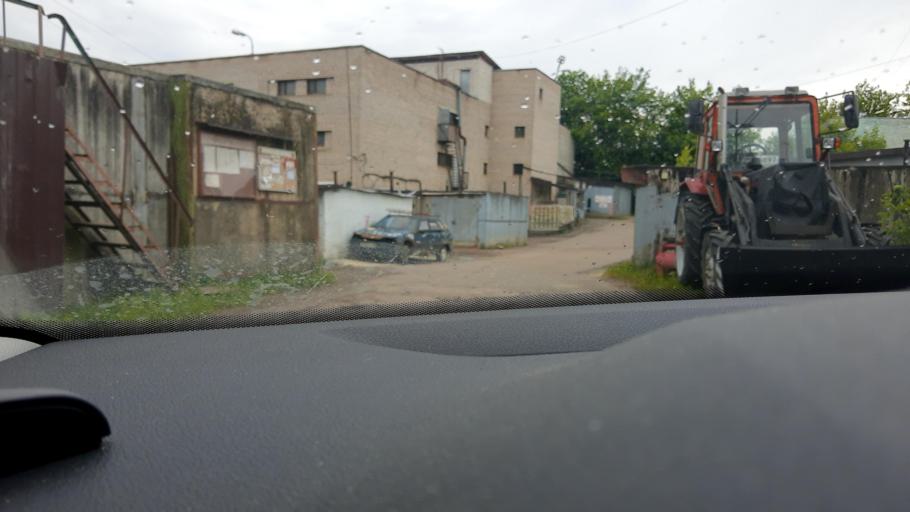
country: RU
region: Moskovskaya
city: Krasnogorsk
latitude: 55.8105
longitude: 37.3218
